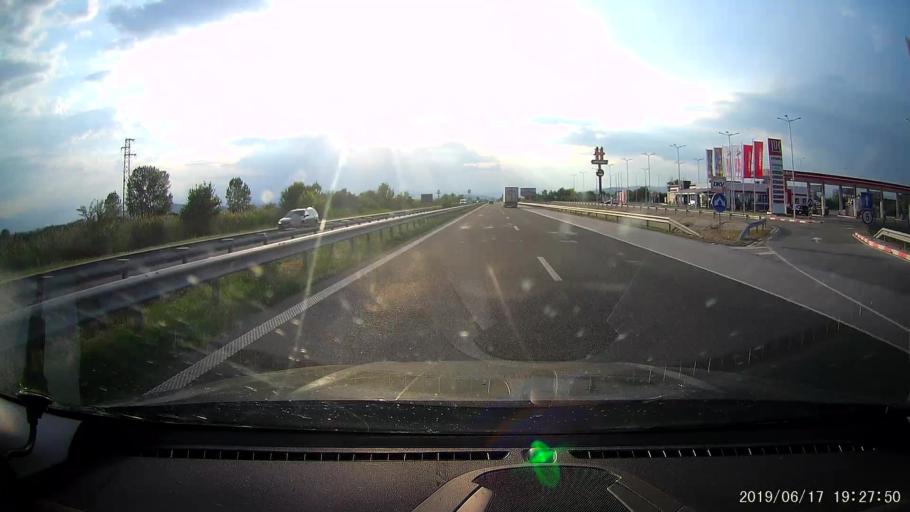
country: BG
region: Pazardzhik
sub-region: Obshtina Pazardzhik
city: Pazardzhik
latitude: 42.2703
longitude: 24.2950
